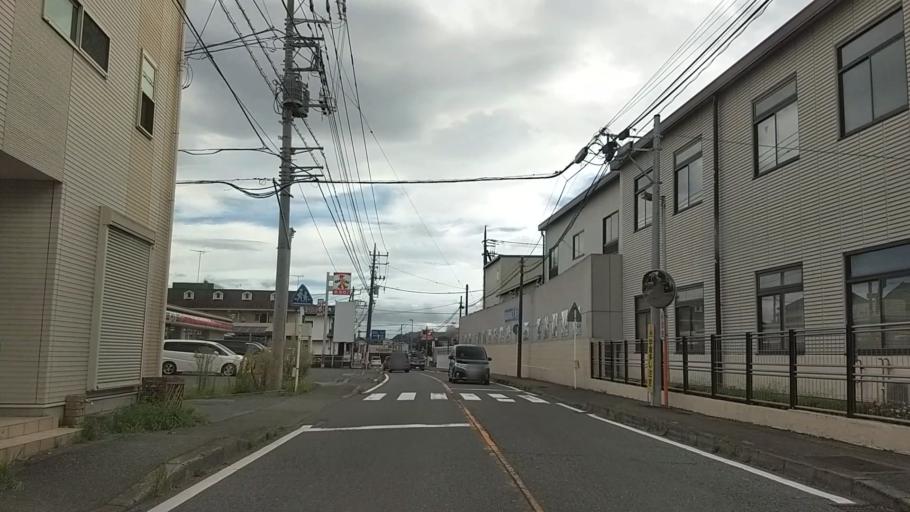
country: JP
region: Tokyo
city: Hachioji
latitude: 35.5997
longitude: 139.3136
